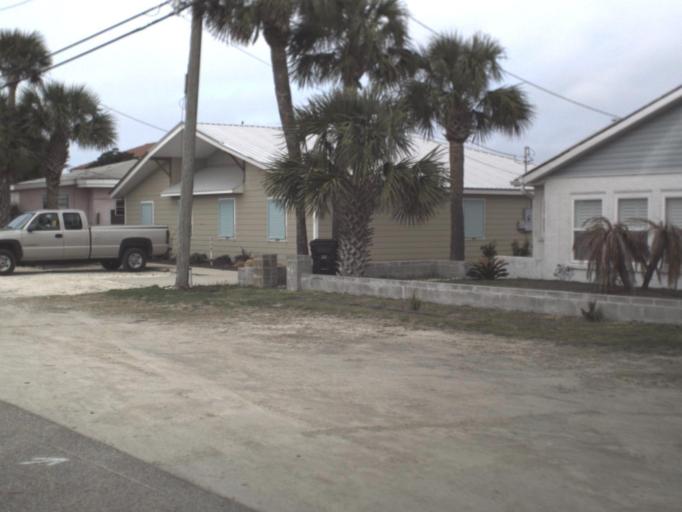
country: US
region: Florida
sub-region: Bay County
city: Laguna Beach
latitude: 30.2459
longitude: -85.9385
